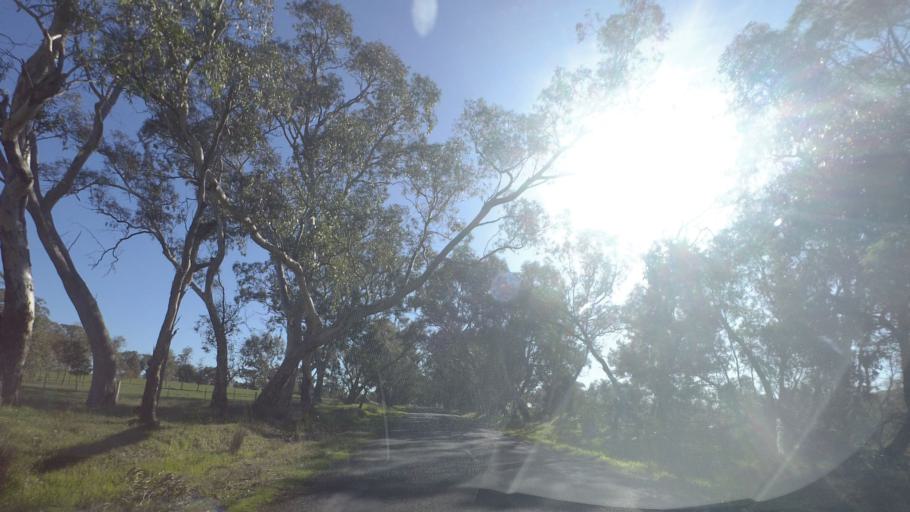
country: AU
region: Victoria
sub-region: Mount Alexander
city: Castlemaine
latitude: -36.9554
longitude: 144.3458
